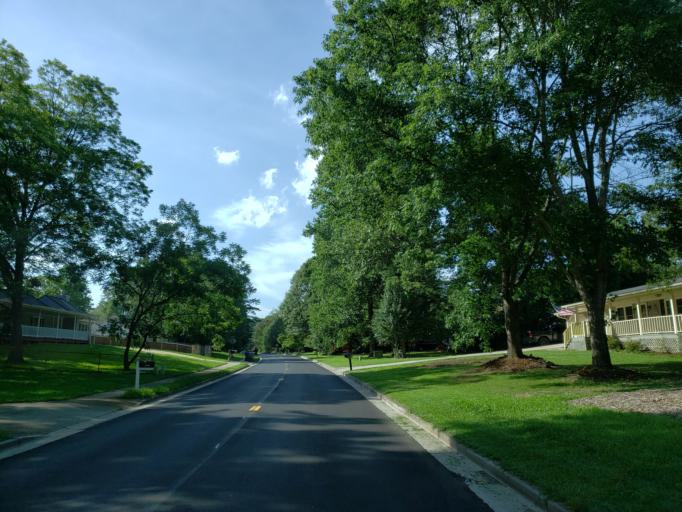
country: US
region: Georgia
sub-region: Cobb County
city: Powder Springs
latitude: 33.9095
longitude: -84.6866
